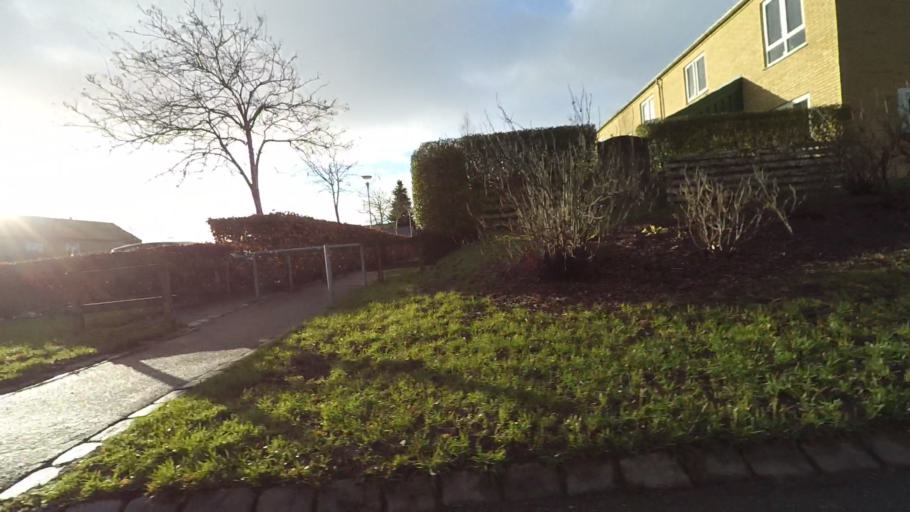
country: DK
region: Central Jutland
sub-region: Arhus Kommune
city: Marslet
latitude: 56.1057
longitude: 10.1703
